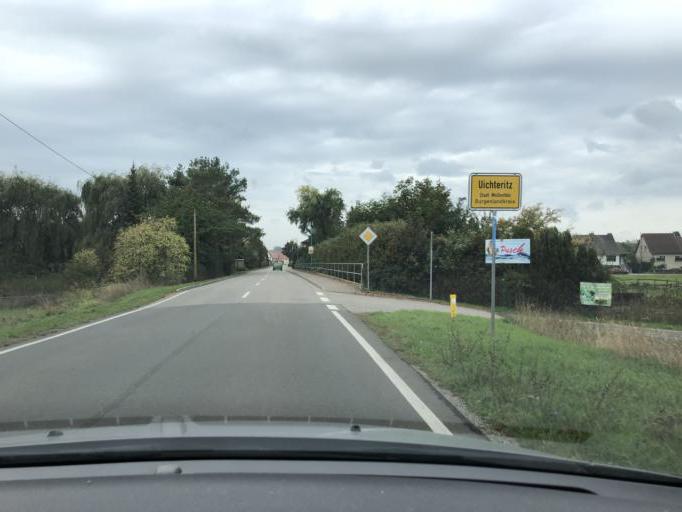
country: DE
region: Saxony-Anhalt
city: Uichteritz
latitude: 51.2092
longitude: 11.9302
